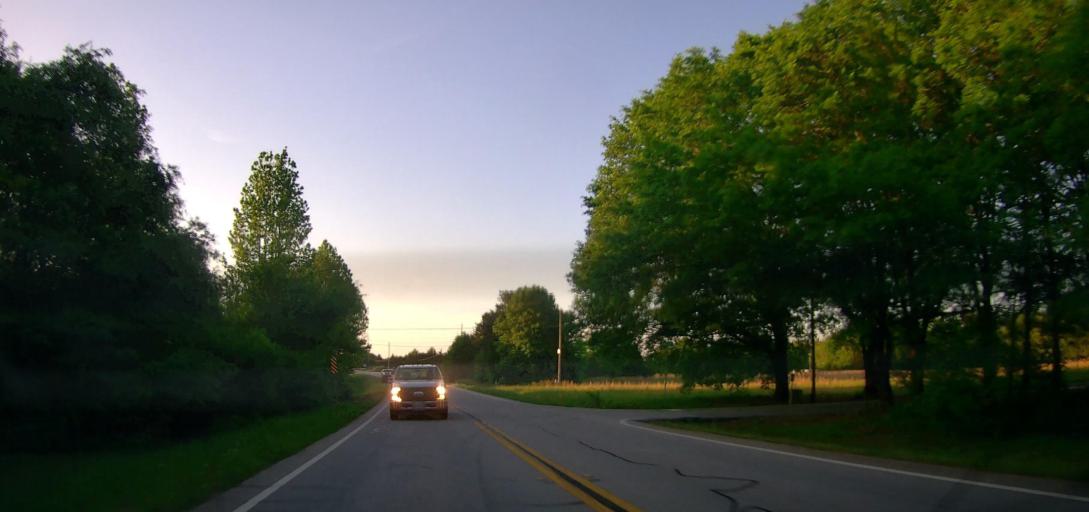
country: US
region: Georgia
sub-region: Newton County
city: Oakwood
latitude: 33.5171
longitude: -83.9485
